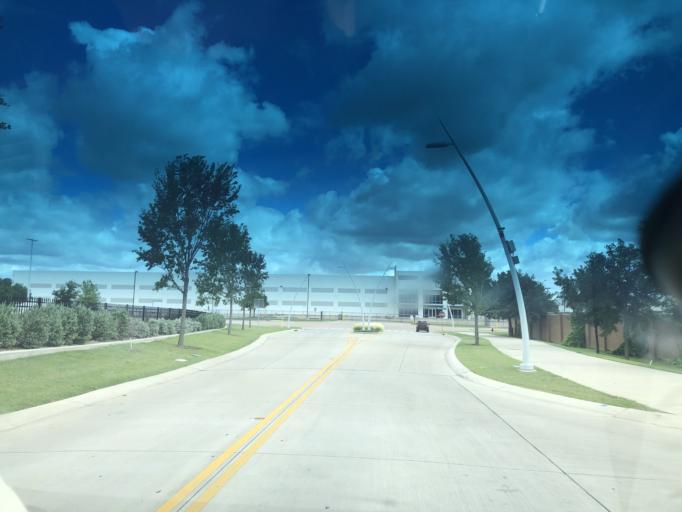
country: US
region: Texas
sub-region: Dallas County
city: Grand Prairie
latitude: 32.7045
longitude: -97.0309
